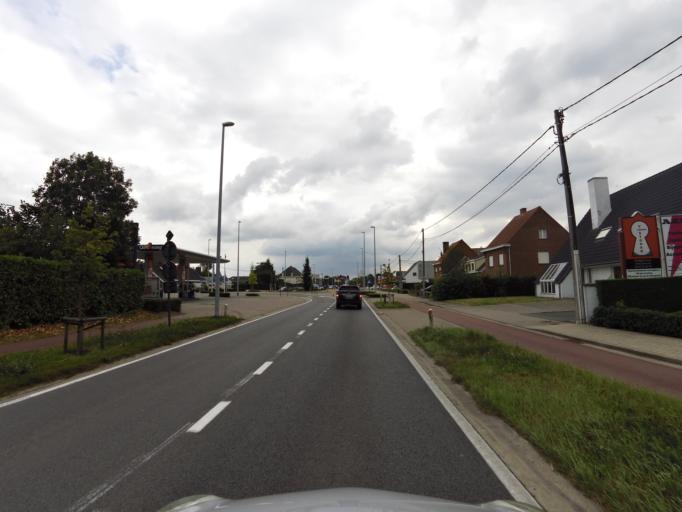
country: BE
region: Flanders
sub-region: Provincie West-Vlaanderen
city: Torhout
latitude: 51.0524
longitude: 3.1038
